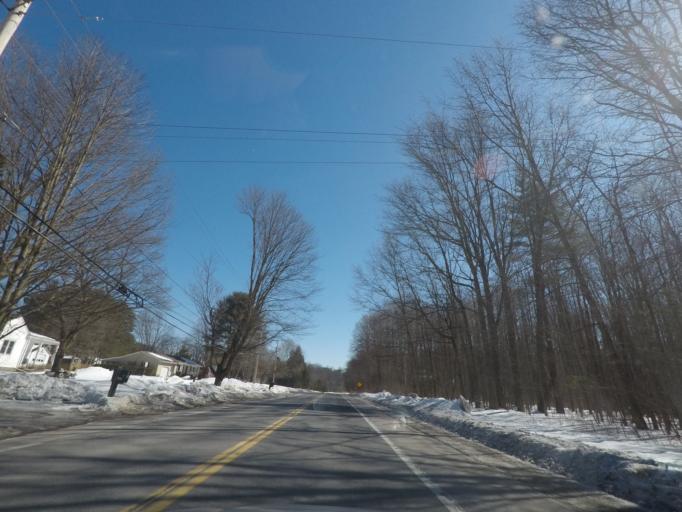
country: US
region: New York
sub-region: Saratoga County
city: Saratoga Springs
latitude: 43.0583
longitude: -73.7826
